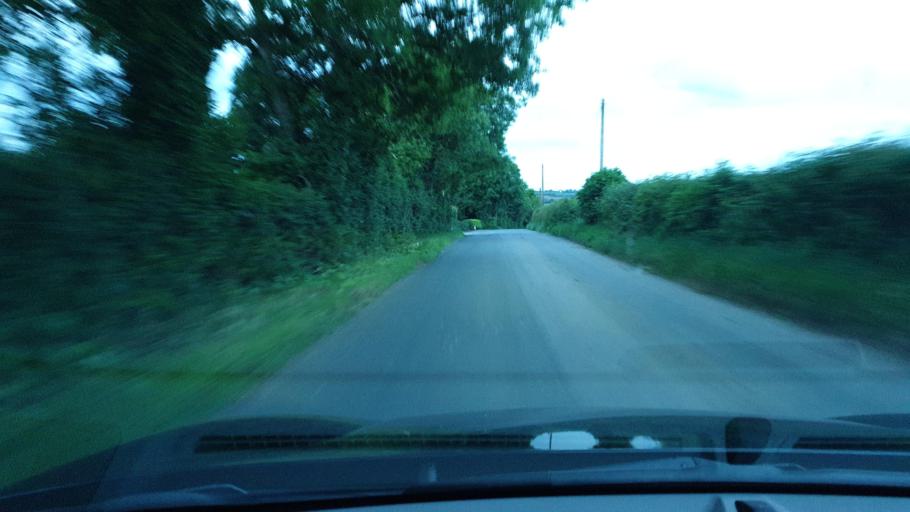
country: IE
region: Leinster
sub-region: An Mhi
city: Ashbourne
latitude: 53.5670
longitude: -6.4125
